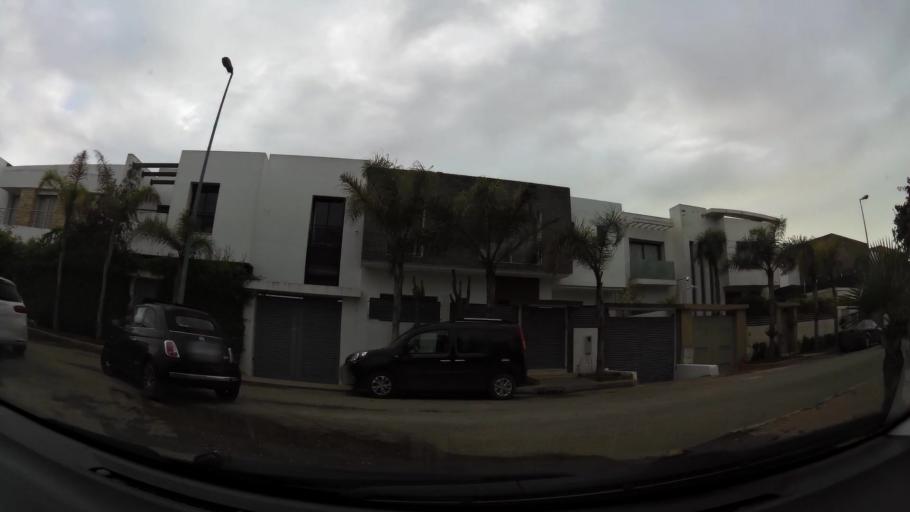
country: MA
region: Grand Casablanca
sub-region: Casablanca
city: Casablanca
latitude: 33.5764
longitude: -7.6798
